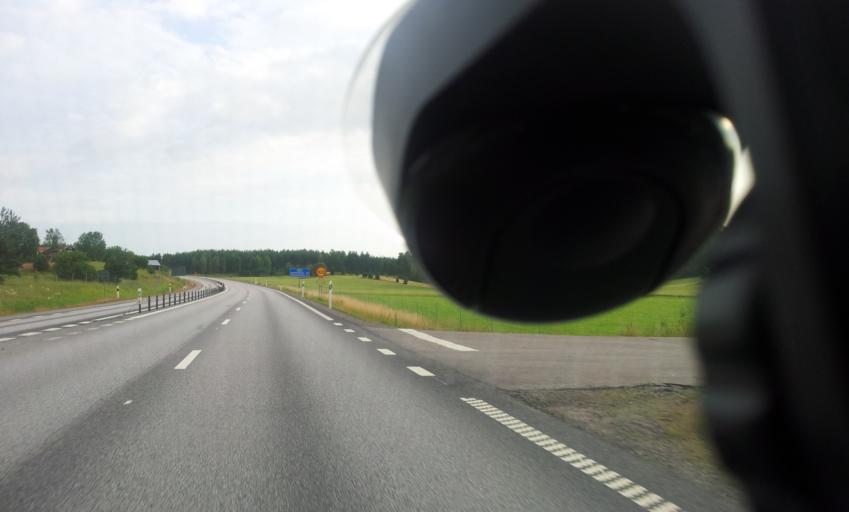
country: SE
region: OEstergoetland
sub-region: Valdemarsviks Kommun
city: Valdemarsvik
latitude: 58.2255
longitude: 16.5527
